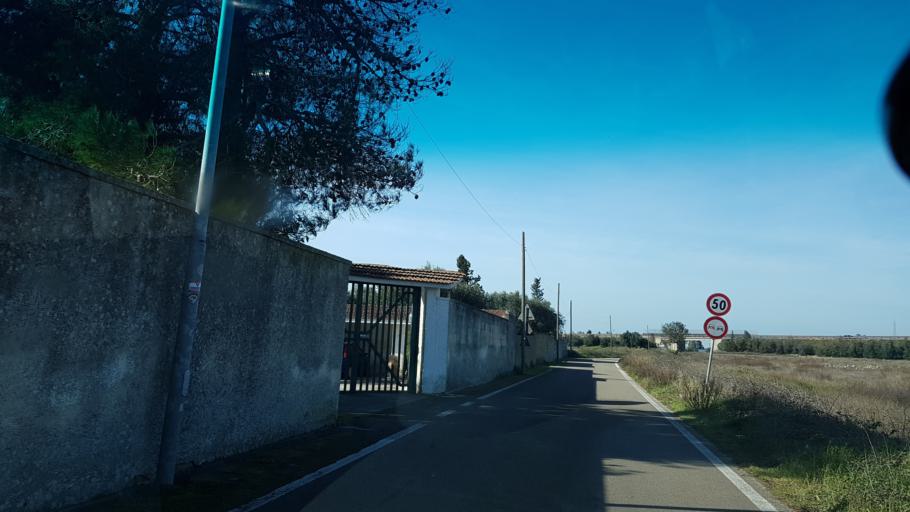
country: IT
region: Apulia
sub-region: Provincia di Lecce
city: Arnesano
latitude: 40.3498
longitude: 18.1305
